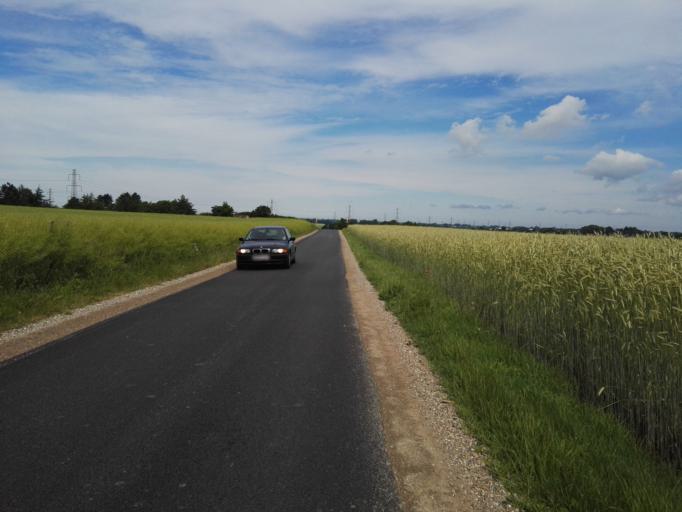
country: DK
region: Capital Region
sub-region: Egedal Kommune
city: Olstykke
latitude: 55.8207
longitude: 12.1679
